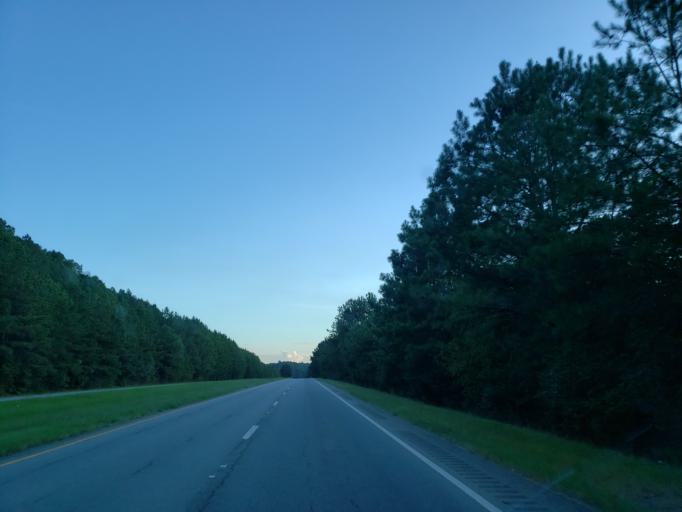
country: US
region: Georgia
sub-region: Floyd County
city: Rome
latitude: 34.2257
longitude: -85.1197
